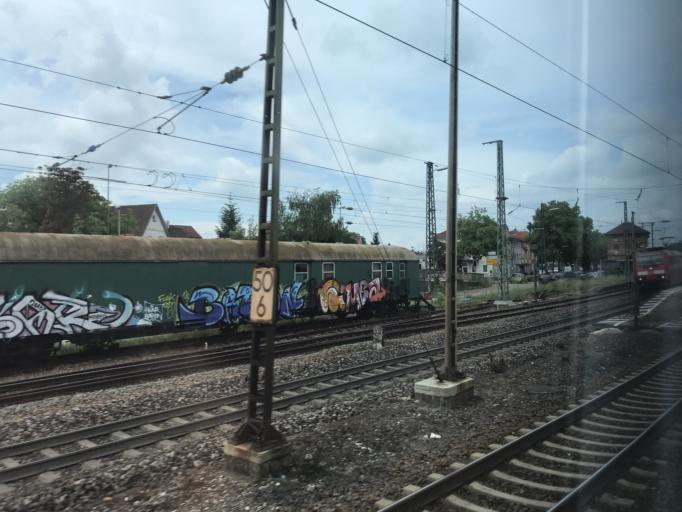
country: DE
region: Baden-Wuerttemberg
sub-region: Regierungsbezirk Stuttgart
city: Sussen
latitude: 48.6823
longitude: 9.7628
